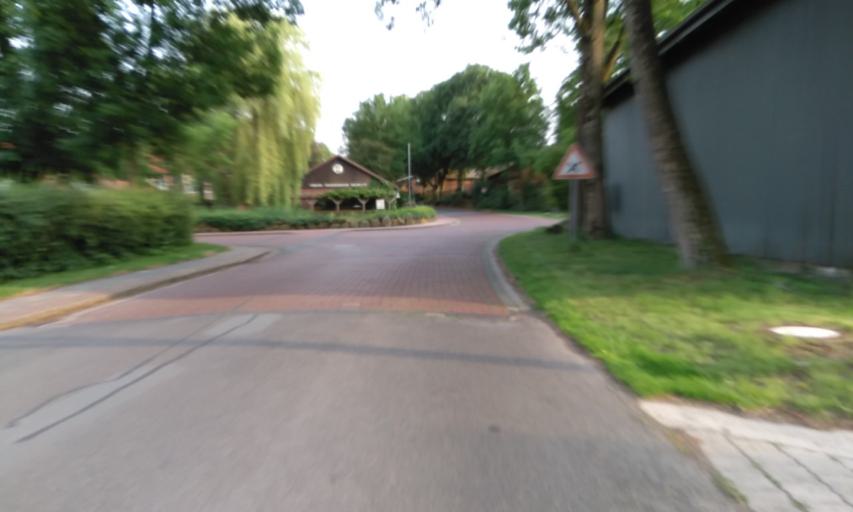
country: DE
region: Lower Saxony
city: Deinste
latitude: 53.5281
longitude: 9.4426
